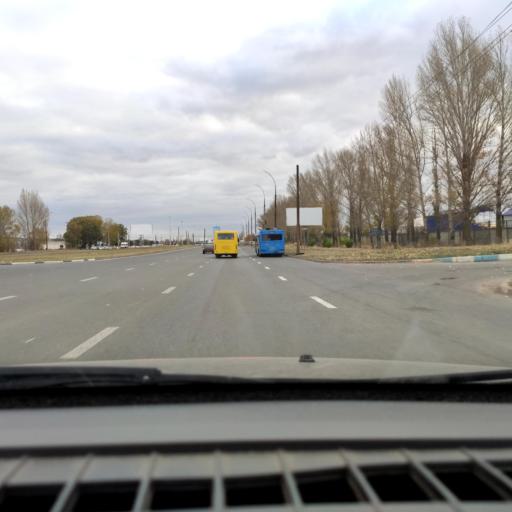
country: RU
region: Samara
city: Podstepki
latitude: 53.5588
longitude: 49.2207
